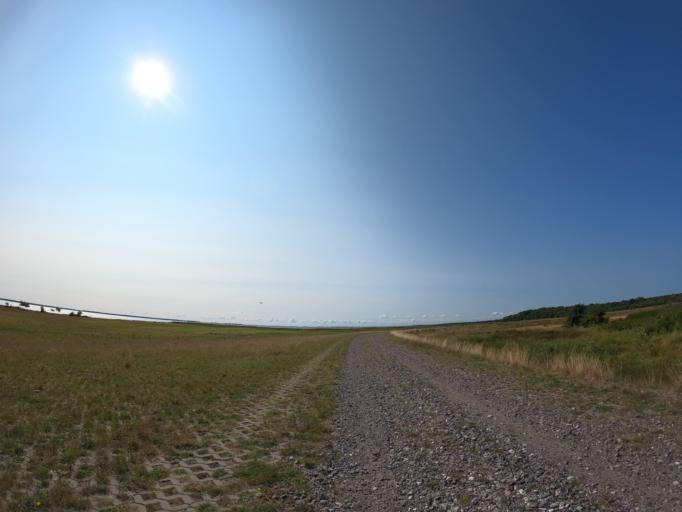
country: DE
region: Mecklenburg-Vorpommern
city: Hiddensee
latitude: 54.5211
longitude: 13.0900
